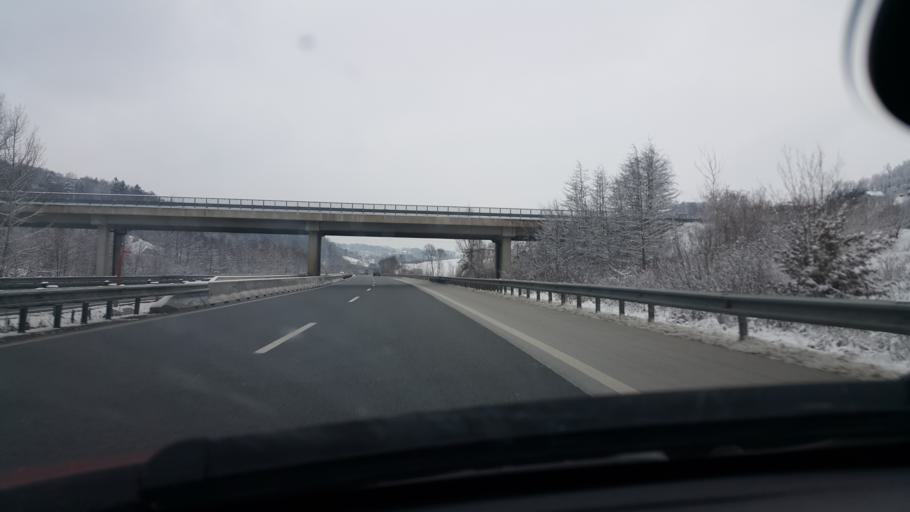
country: SI
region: Pesnica
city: Pesnica pri Mariboru
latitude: 46.6371
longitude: 15.6555
